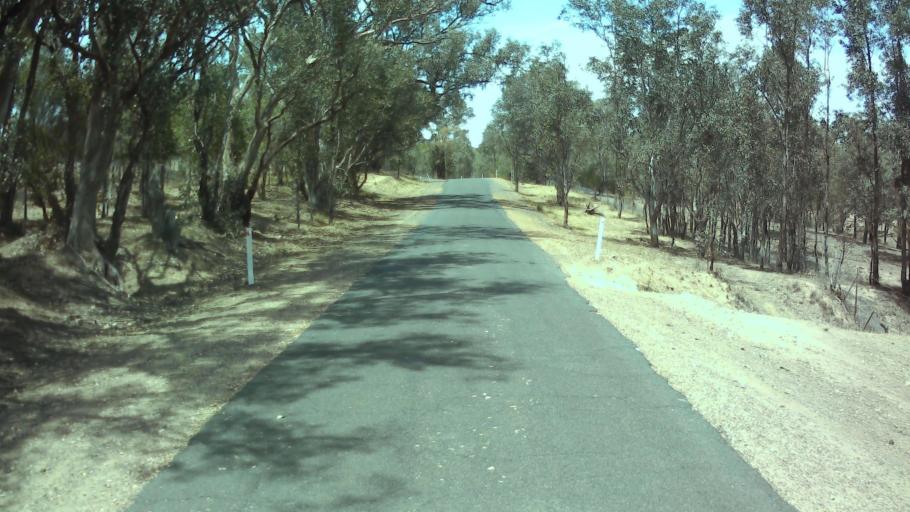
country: AU
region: New South Wales
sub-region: Weddin
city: Grenfell
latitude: -34.0260
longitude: 148.4317
